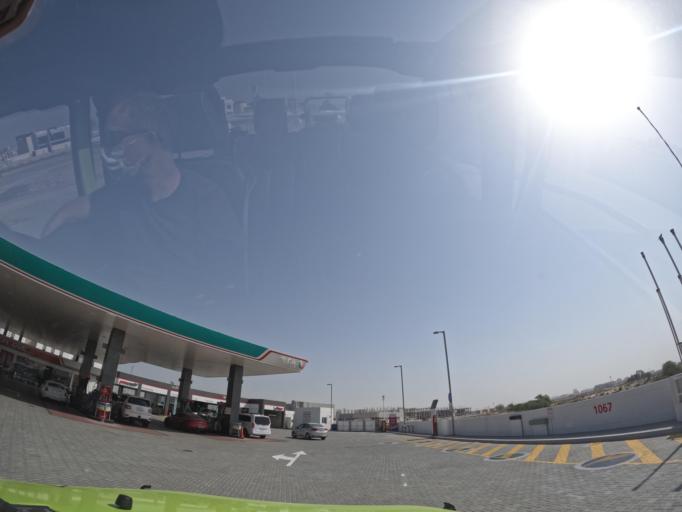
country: AE
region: Ash Shariqah
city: Sharjah
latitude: 25.1586
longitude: 55.3639
